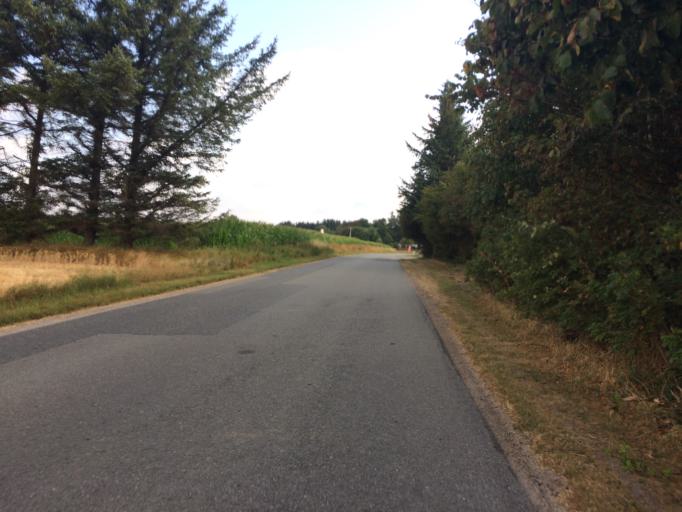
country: DK
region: Central Jutland
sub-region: Holstebro Kommune
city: Vinderup
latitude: 56.6165
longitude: 8.7337
